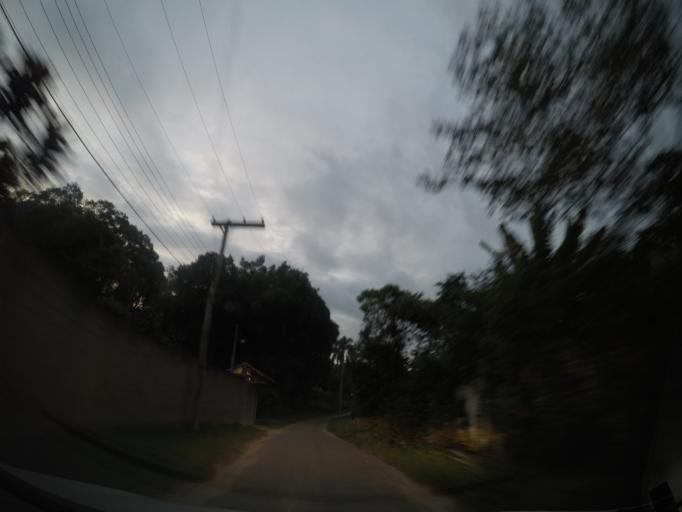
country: BR
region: Sao Paulo
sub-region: Aruja
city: Aruja
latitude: -23.3481
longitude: -46.2898
